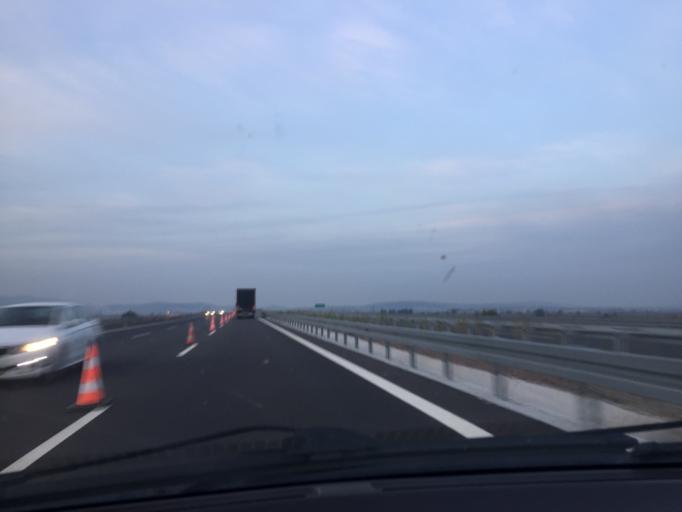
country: TR
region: Manisa
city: Halitpasa
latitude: 38.7331
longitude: 27.6562
